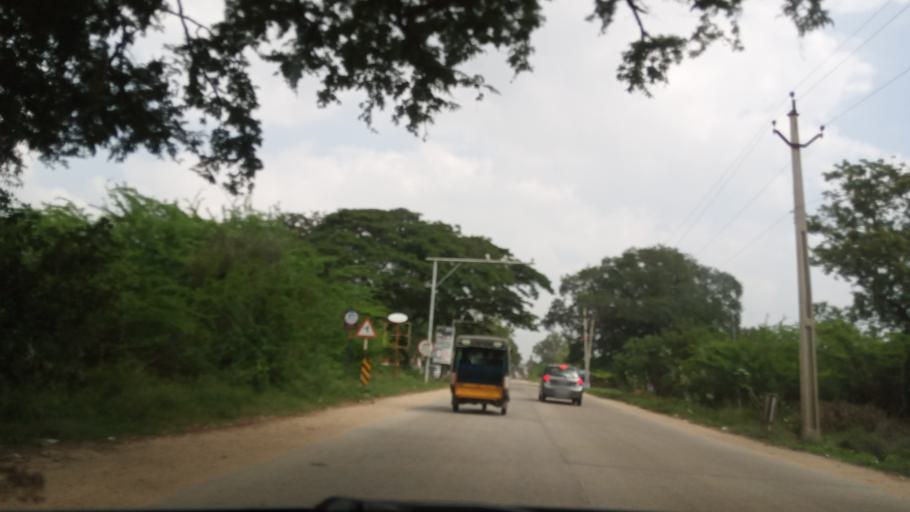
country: IN
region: Andhra Pradesh
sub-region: Chittoor
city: Madanapalle
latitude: 13.6347
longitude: 78.6241
